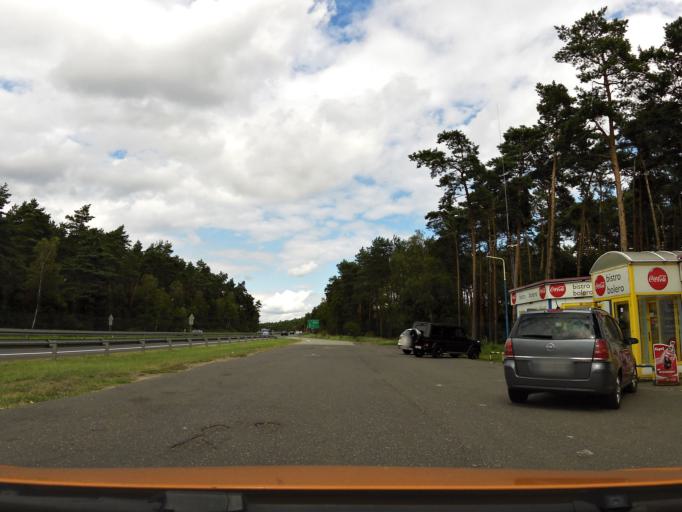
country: PL
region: West Pomeranian Voivodeship
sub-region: Powiat goleniowski
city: Goleniow
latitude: 53.5238
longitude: 14.8090
